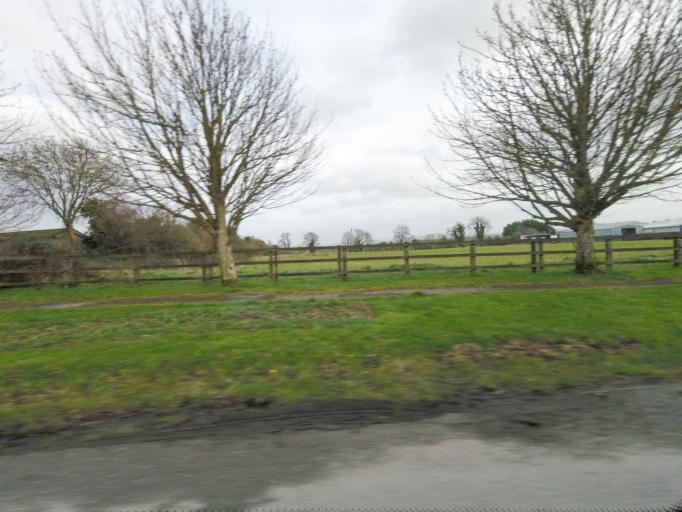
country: IE
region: Leinster
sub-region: Kildare
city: Kilcullen
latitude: 53.1390
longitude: -6.7377
